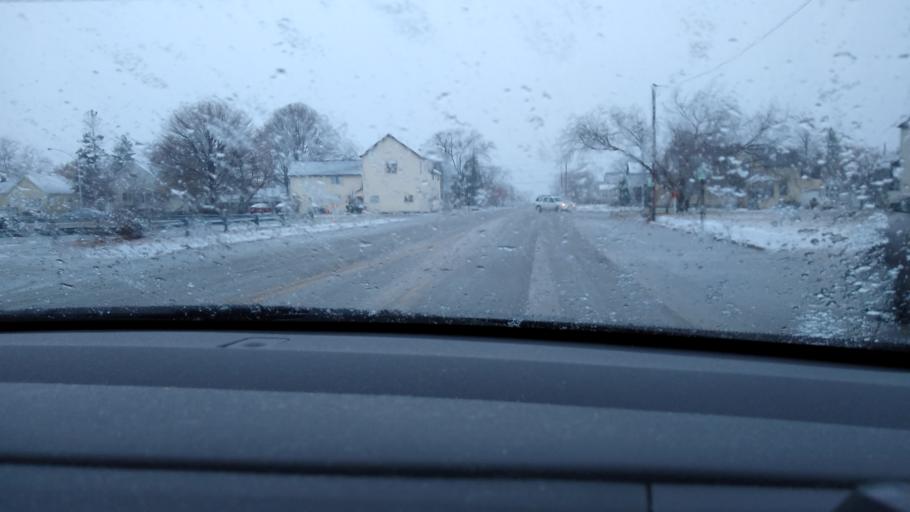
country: US
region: Michigan
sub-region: Delta County
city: Escanaba
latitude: 45.7462
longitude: -87.0612
